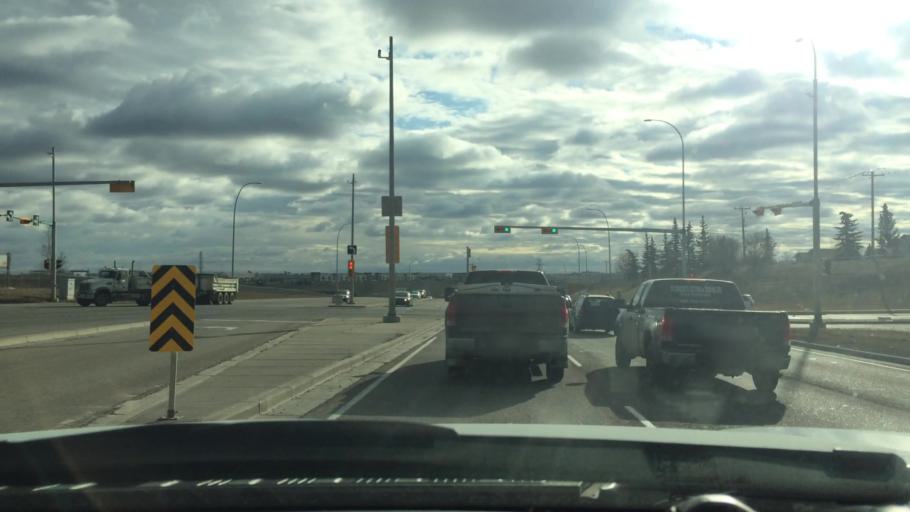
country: CA
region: Alberta
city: Calgary
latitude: 51.1282
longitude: -114.0538
